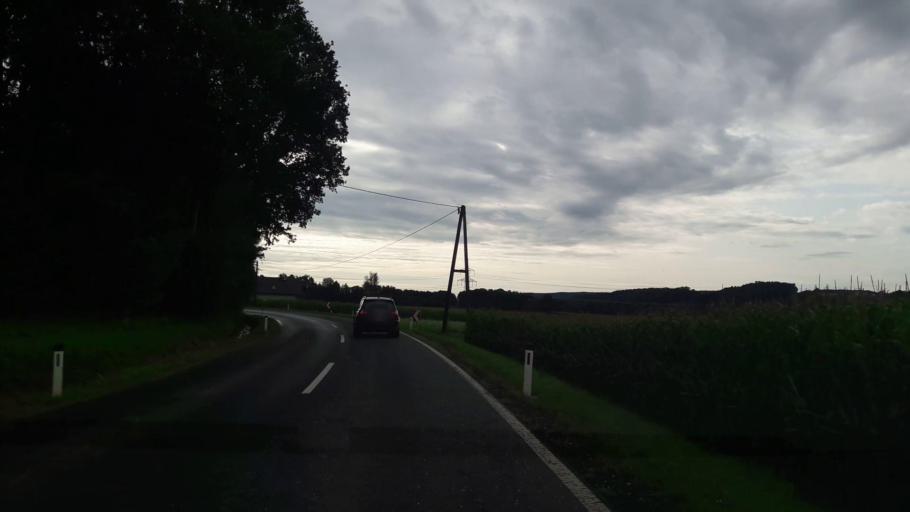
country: AT
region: Styria
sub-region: Politischer Bezirk Hartberg-Fuerstenfeld
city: Ebersdorf
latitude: 47.2094
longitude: 15.9386
